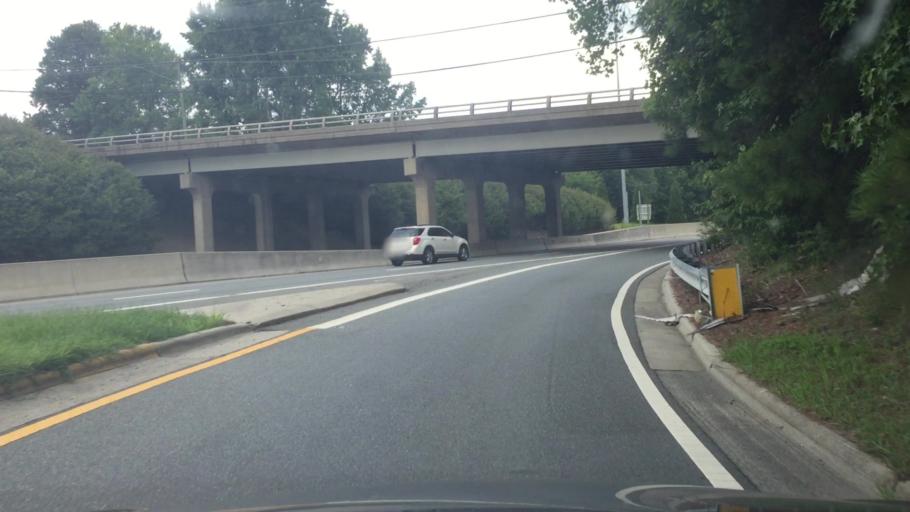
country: US
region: North Carolina
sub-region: Randolph County
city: Asheboro
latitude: 35.6873
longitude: -79.8304
